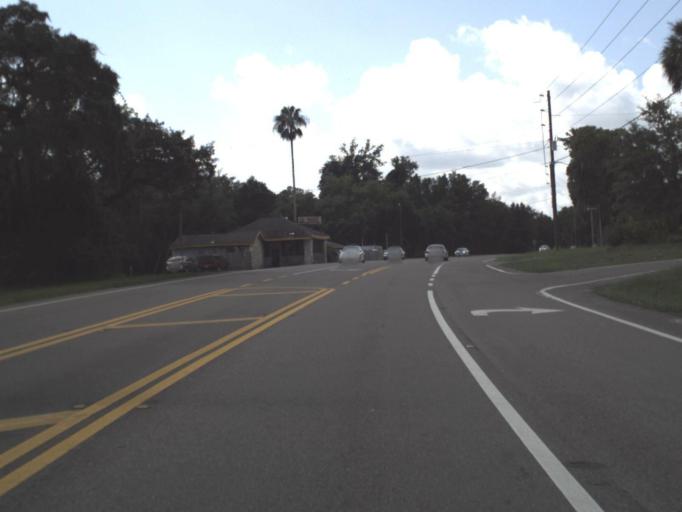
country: US
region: Florida
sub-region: Citrus County
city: Floral City
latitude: 28.7778
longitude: -82.2947
